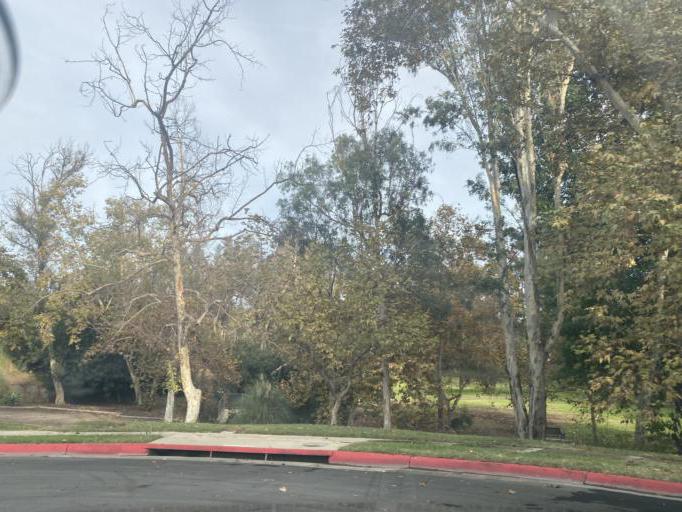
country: US
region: California
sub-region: Orange County
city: Brea
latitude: 33.9030
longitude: -117.8766
